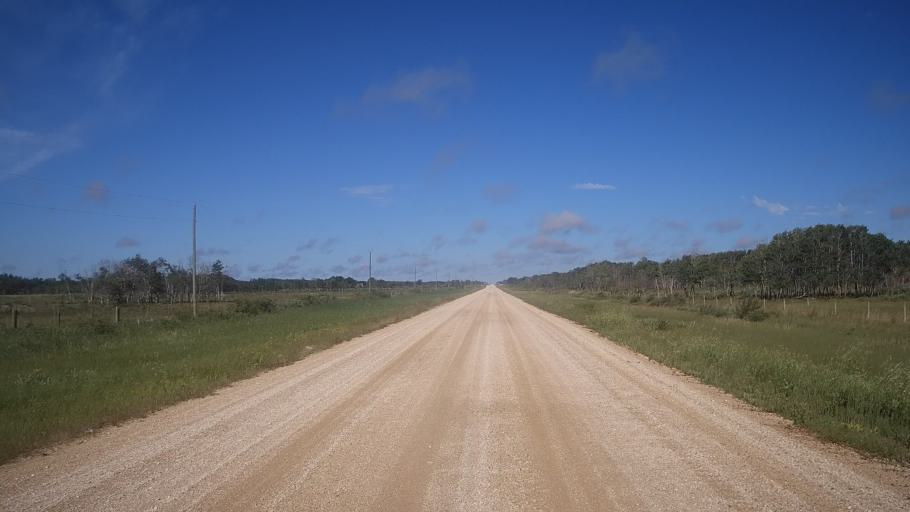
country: CA
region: Manitoba
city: Stonewall
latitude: 50.2411
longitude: -97.7214
